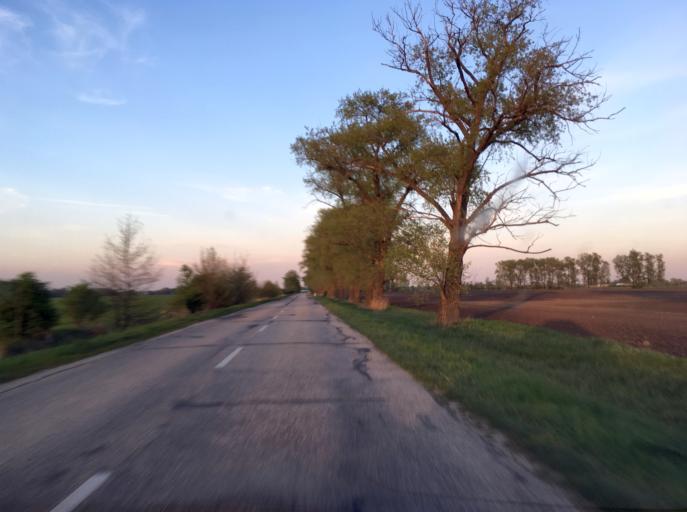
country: SK
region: Nitriansky
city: Kolarovo
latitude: 47.9023
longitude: 17.9402
